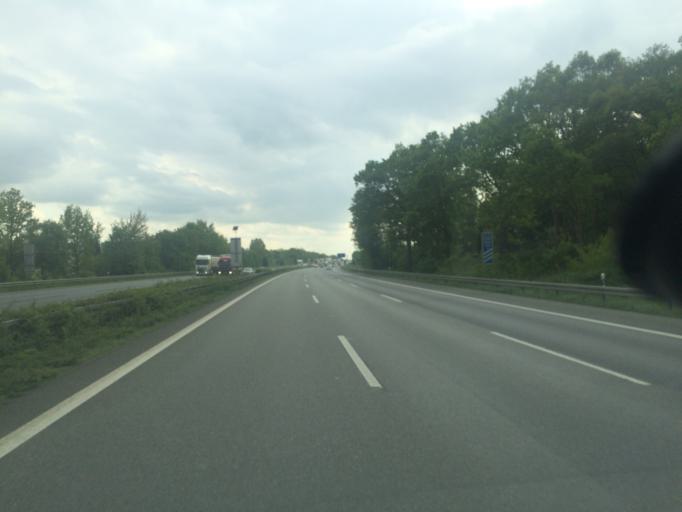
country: DE
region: North Rhine-Westphalia
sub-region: Regierungsbezirk Detmold
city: Guetersloh
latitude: 51.8874
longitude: 8.4414
